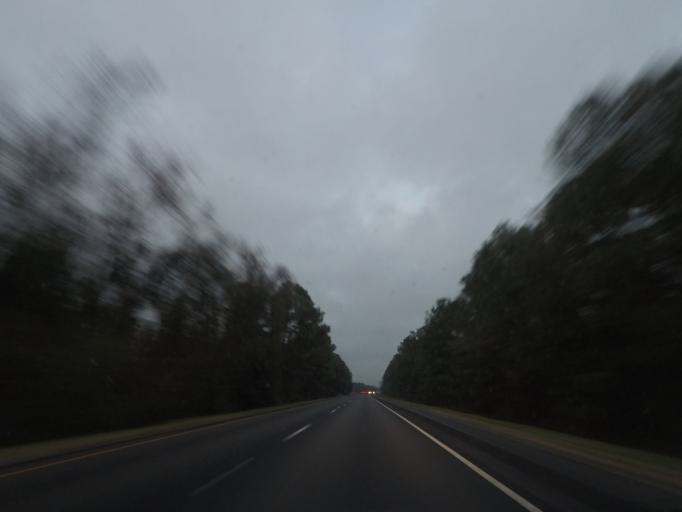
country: US
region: South Carolina
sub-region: Clarendon County
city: Manning
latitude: 33.7890
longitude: -80.1667
